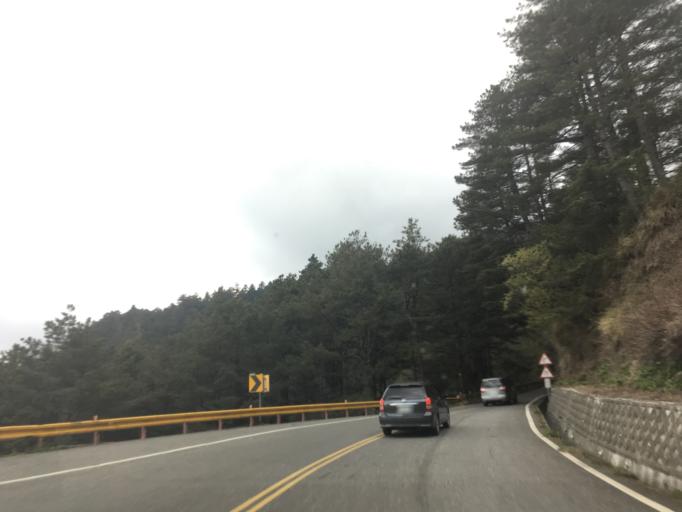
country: TW
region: Taiwan
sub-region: Hualien
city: Hualian
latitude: 24.1785
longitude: 121.3043
